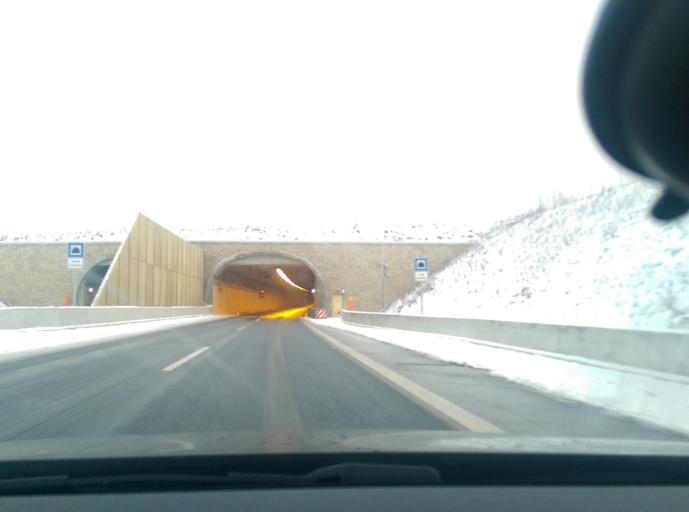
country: DE
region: Hesse
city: Hessisch Lichtenau
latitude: 51.2027
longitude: 9.7401
